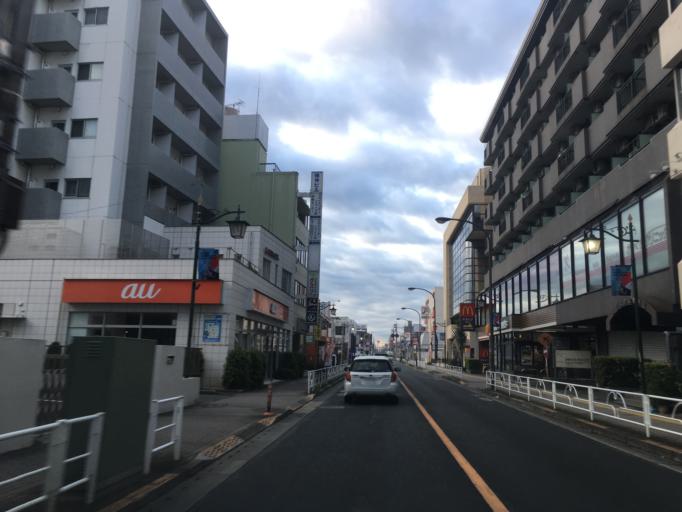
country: JP
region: Tokyo
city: Higashimurayama-shi
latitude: 35.7605
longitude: 139.4672
